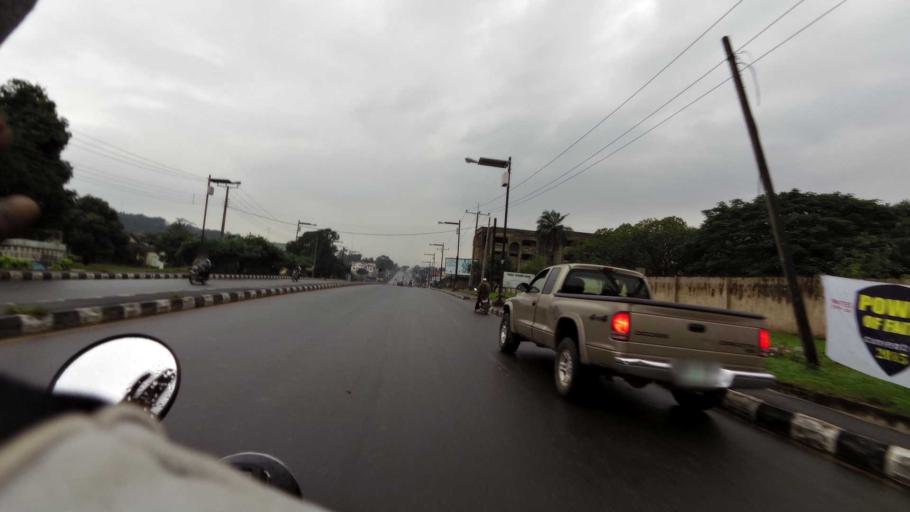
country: NG
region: Oyo
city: Ibadan
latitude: 7.3983
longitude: 3.9099
